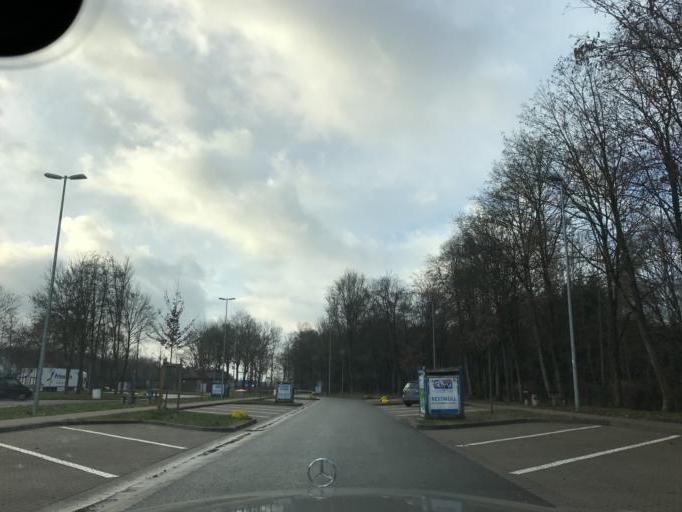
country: DE
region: Lower Saxony
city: Gyhum
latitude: 53.2023
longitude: 9.2966
